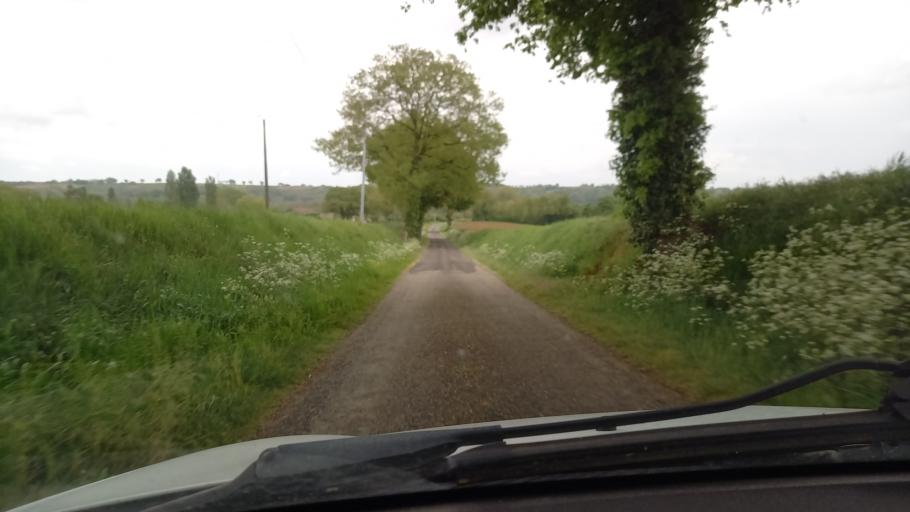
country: FR
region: Midi-Pyrenees
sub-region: Departement du Gers
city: Gimont
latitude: 43.7582
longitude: 0.8584
